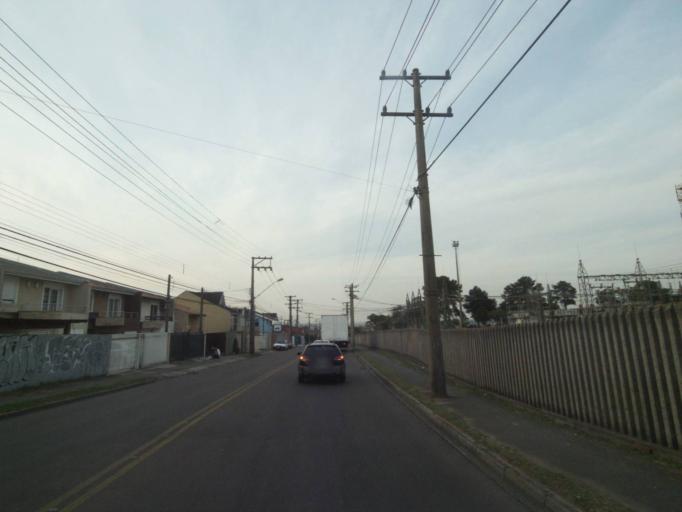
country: BR
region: Parana
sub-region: Pinhais
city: Pinhais
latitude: -25.4768
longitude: -49.2097
